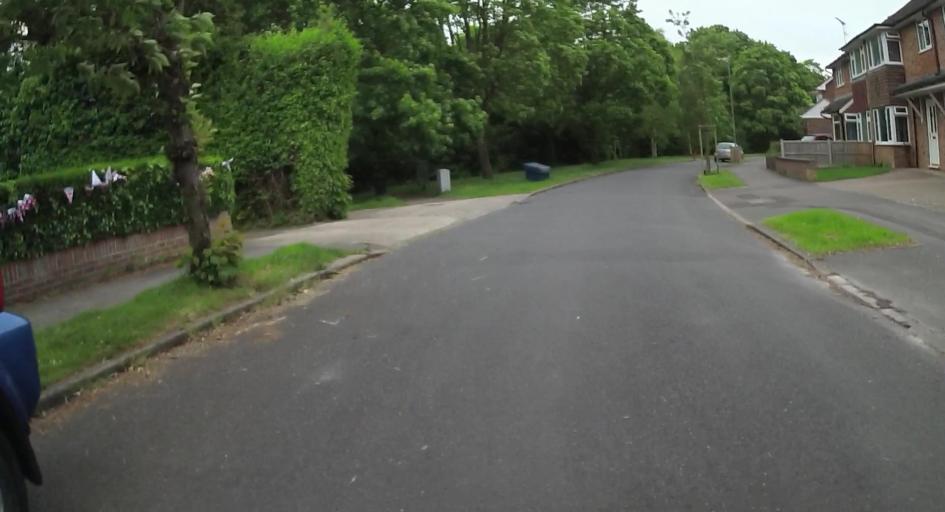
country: GB
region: England
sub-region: Hampshire
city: Basingstoke
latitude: 51.2499
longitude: -1.0921
